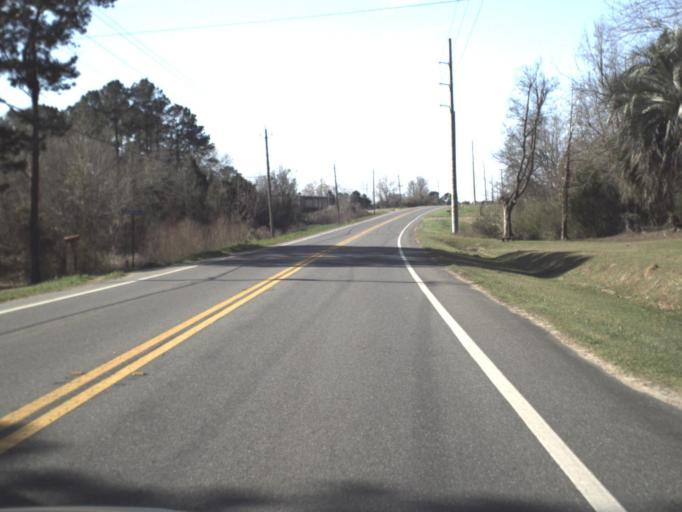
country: US
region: Florida
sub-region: Jackson County
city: Marianna
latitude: 30.7866
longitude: -85.1866
